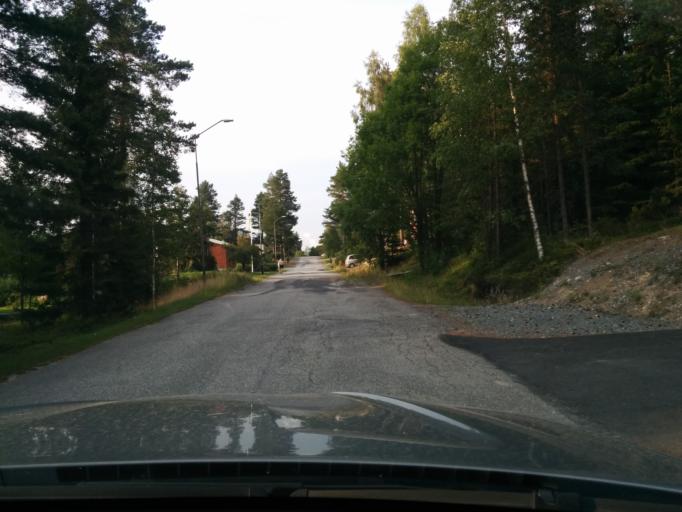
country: SE
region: Vaesternorrland
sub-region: OErnskoeldsviks Kommun
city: Ornskoldsvik
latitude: 63.2589
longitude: 18.6904
